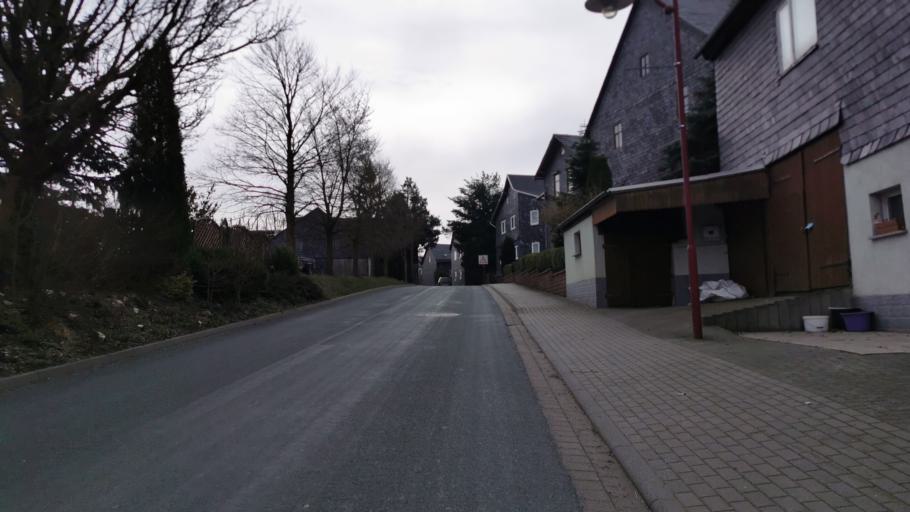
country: DE
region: Thuringia
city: Leutenberg
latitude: 50.5174
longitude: 11.4511
